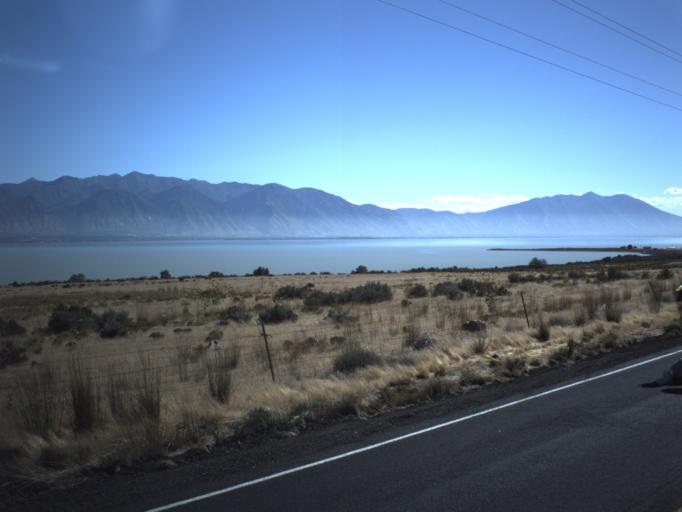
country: US
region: Utah
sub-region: Utah County
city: Saratoga Springs
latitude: 40.2778
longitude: -111.8691
